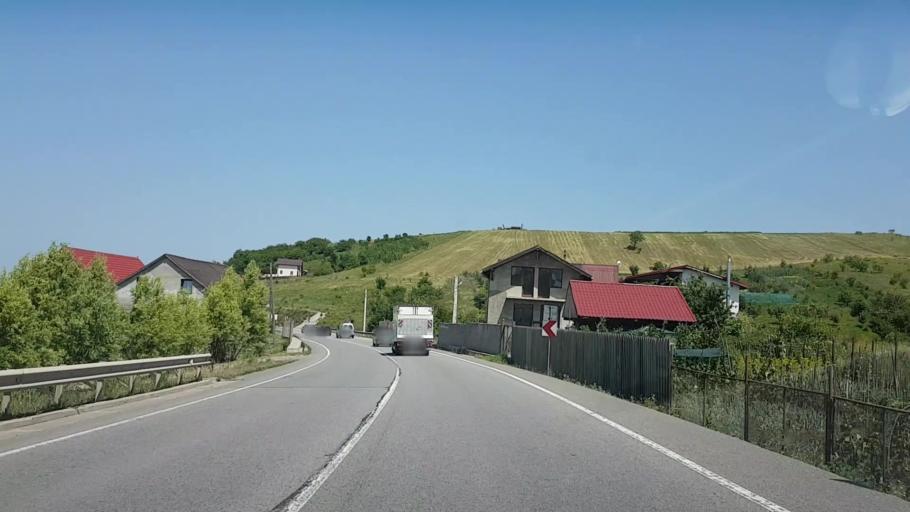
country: RO
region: Cluj
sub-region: Comuna Apahida
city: Dezmir
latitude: 46.7710
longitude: 23.6988
